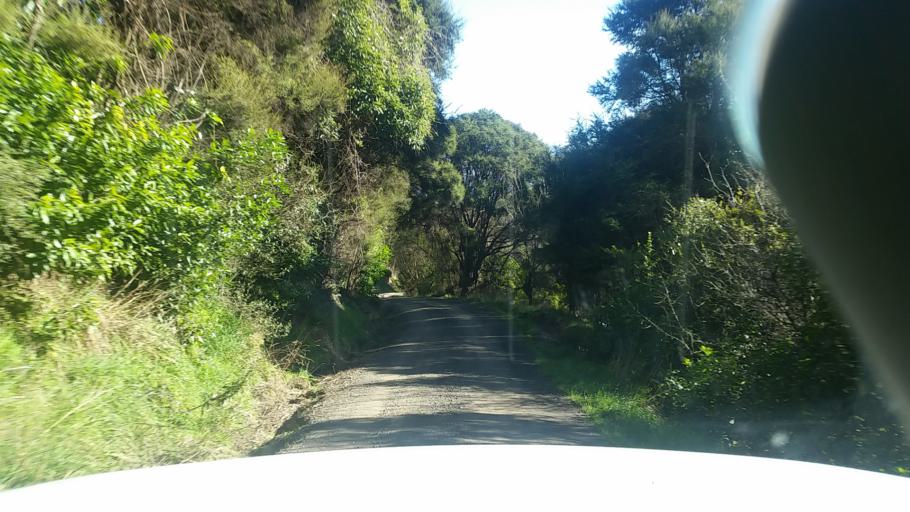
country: NZ
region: Canterbury
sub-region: Christchurch City
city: Christchurch
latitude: -43.7912
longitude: 172.9900
